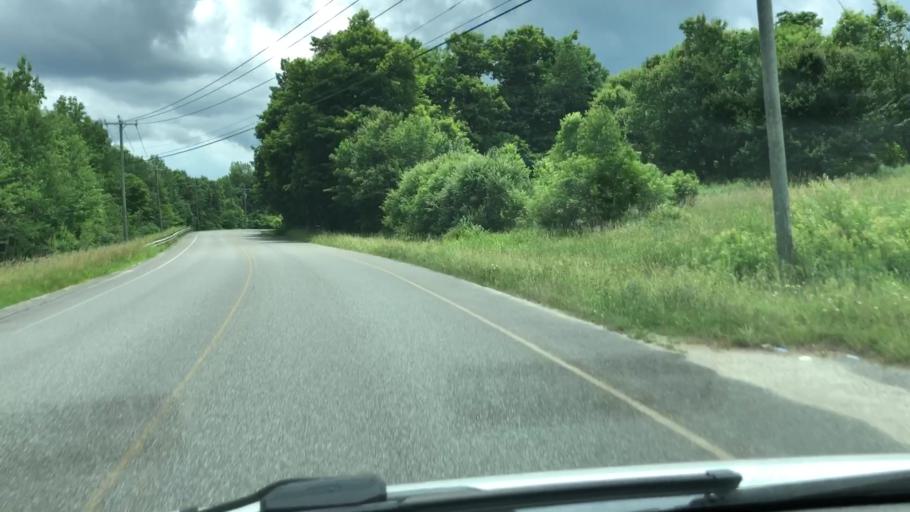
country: US
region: Massachusetts
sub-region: Berkshire County
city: Adams
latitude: 42.5434
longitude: -73.0533
